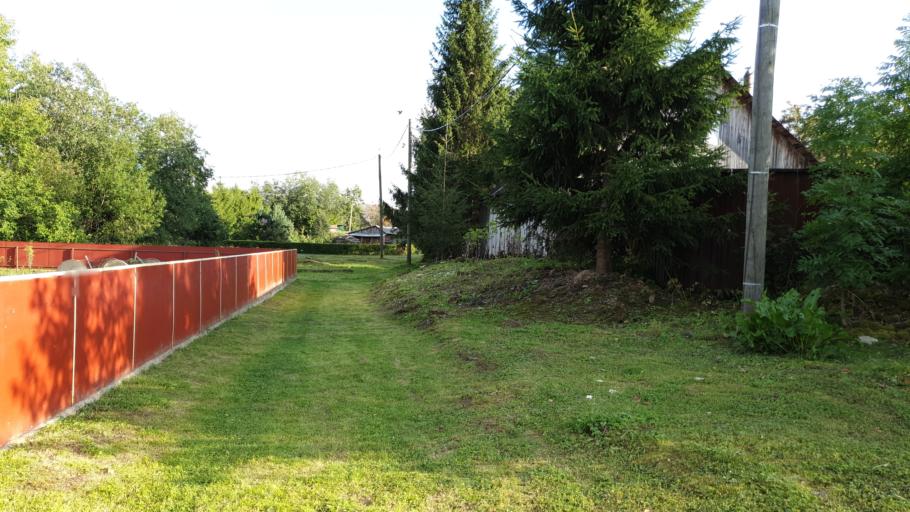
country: RU
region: Leningrad
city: Ivangorod
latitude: 59.4295
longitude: 28.3216
